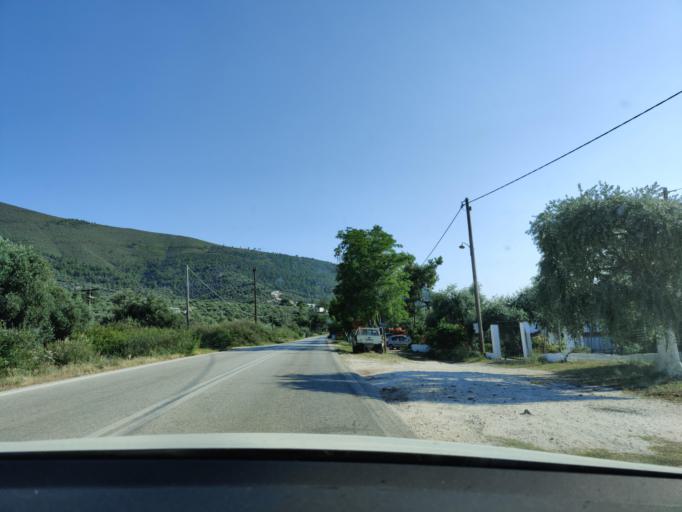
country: GR
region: East Macedonia and Thrace
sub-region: Nomos Kavalas
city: Prinos
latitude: 40.6877
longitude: 24.5266
